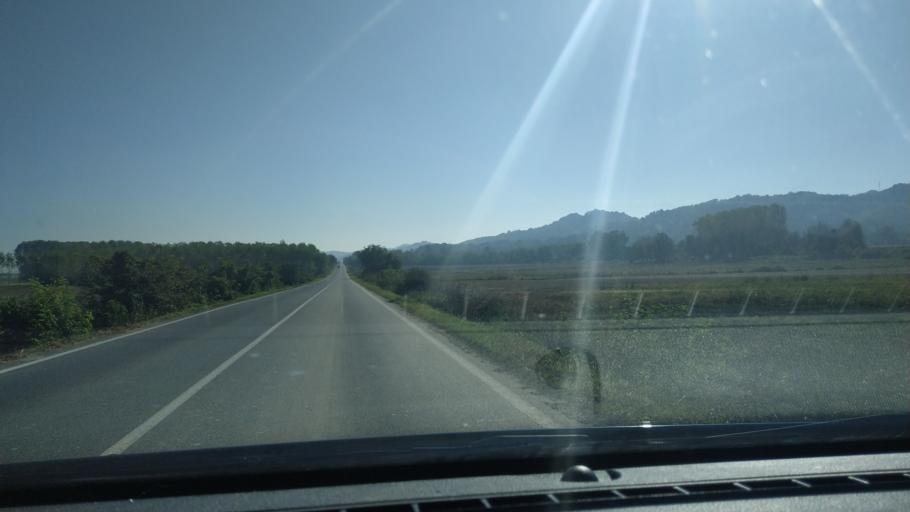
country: IT
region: Piedmont
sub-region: Provincia di Torino
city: Monteu da Po
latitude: 45.1620
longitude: 8.0085
